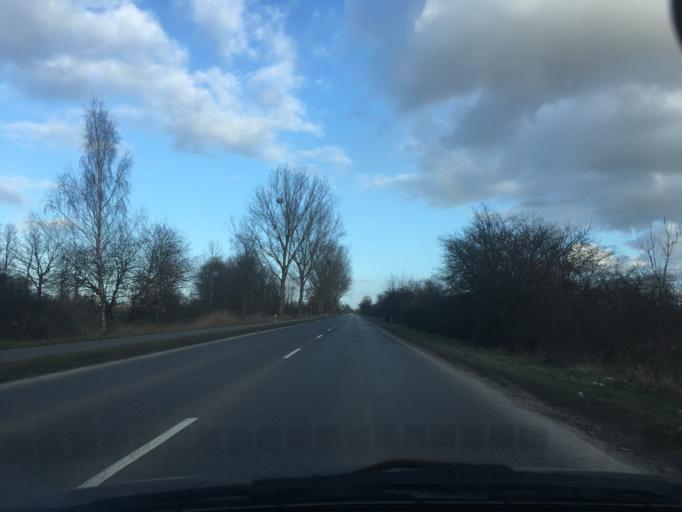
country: PL
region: Pomeranian Voivodeship
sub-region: Gdansk
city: Gdansk
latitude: 54.3276
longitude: 18.7551
